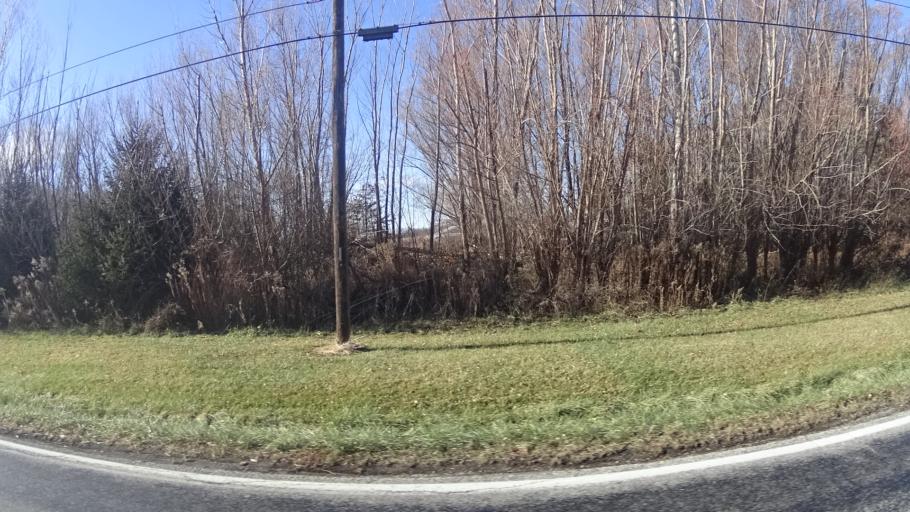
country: US
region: Ohio
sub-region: Lorain County
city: South Amherst
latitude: 41.3451
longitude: -82.2999
